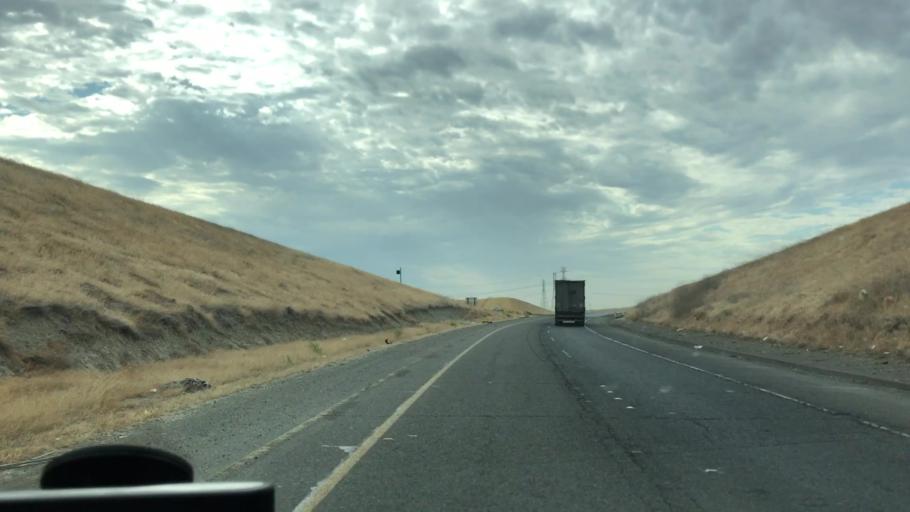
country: US
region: California
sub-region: San Joaquin County
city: Mountain House
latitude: 37.7397
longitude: -121.5587
